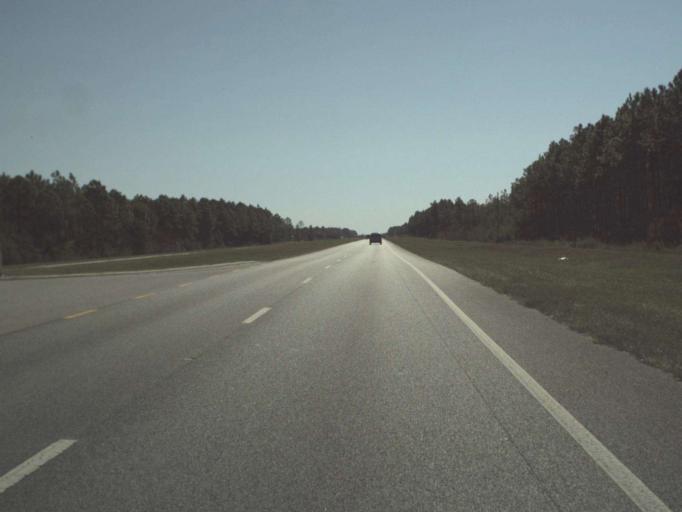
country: US
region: Florida
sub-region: Walton County
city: Seaside
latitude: 30.3023
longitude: -86.0303
